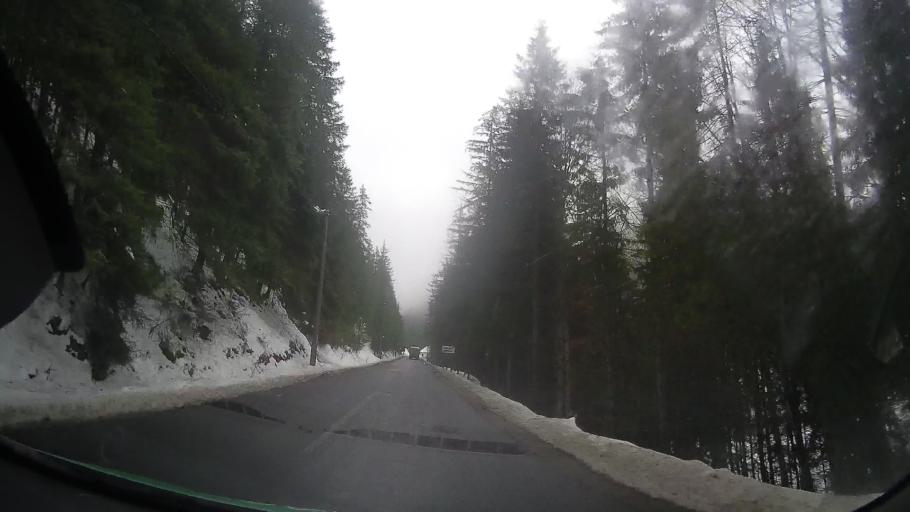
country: RO
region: Neamt
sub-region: Comuna Bicaz Chei
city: Bicaz Chei
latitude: 46.7821
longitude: 25.7859
